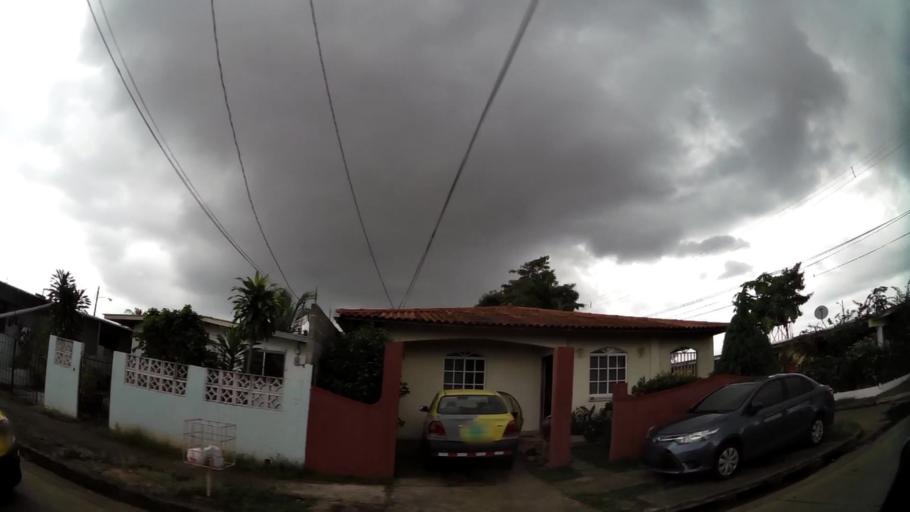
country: PA
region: Panama
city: Tocumen
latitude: 9.0567
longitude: -79.4162
